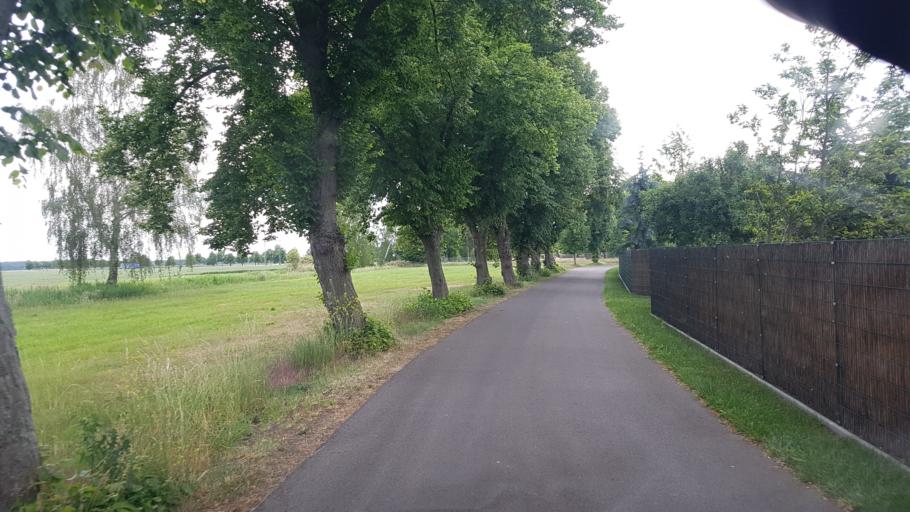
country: DE
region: Saxony-Anhalt
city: Holzdorf
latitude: 51.8133
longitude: 13.2329
